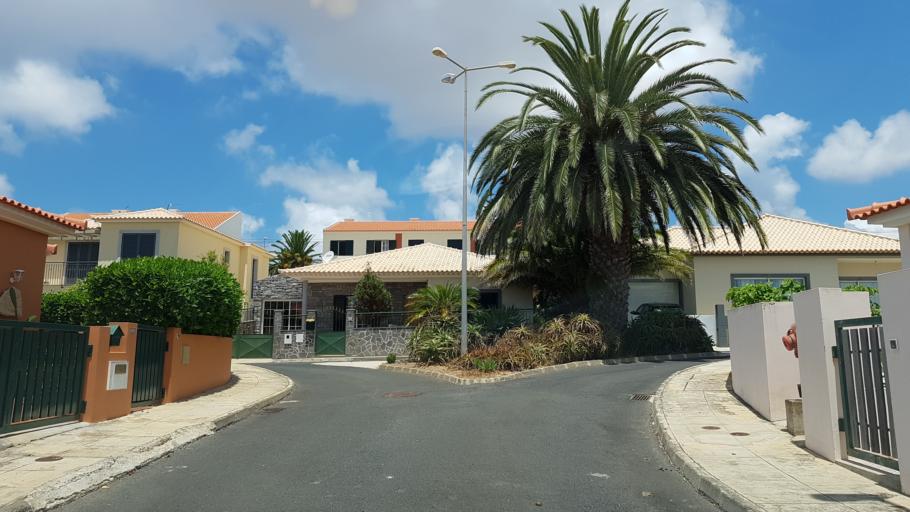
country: PT
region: Madeira
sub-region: Porto Santo
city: Vila de Porto Santo
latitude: 33.0616
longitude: -16.3561
